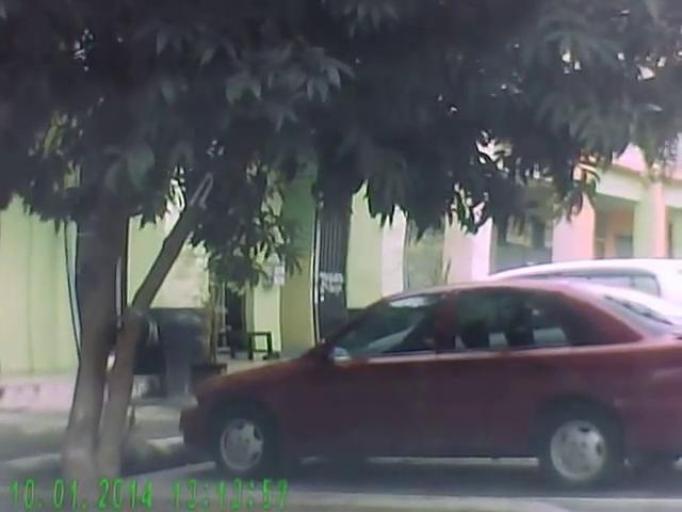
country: MY
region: Selangor
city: Klang
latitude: 3.0661
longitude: 101.4719
